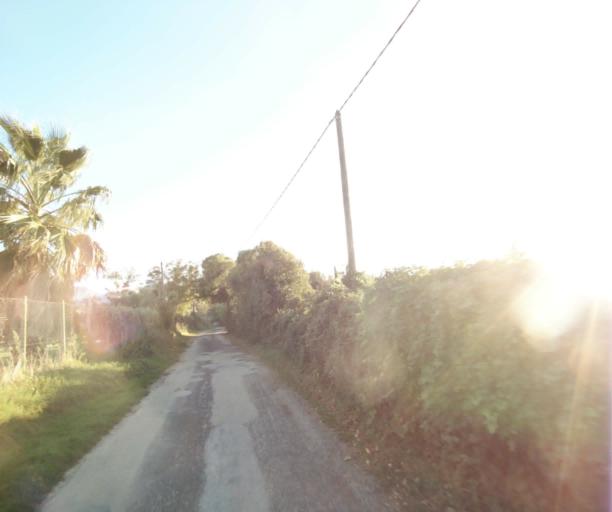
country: FR
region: Languedoc-Roussillon
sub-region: Departement des Pyrenees-Orientales
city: Elne
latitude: 42.5783
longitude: 2.9868
